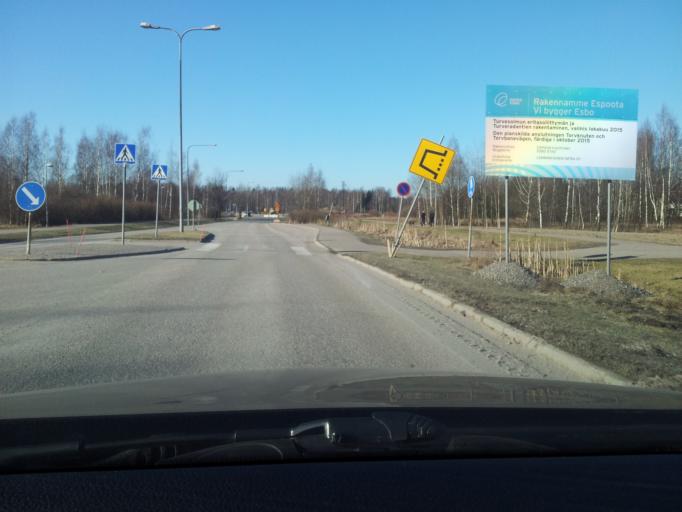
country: FI
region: Uusimaa
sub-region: Helsinki
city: Koukkuniemi
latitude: 60.1828
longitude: 24.7785
